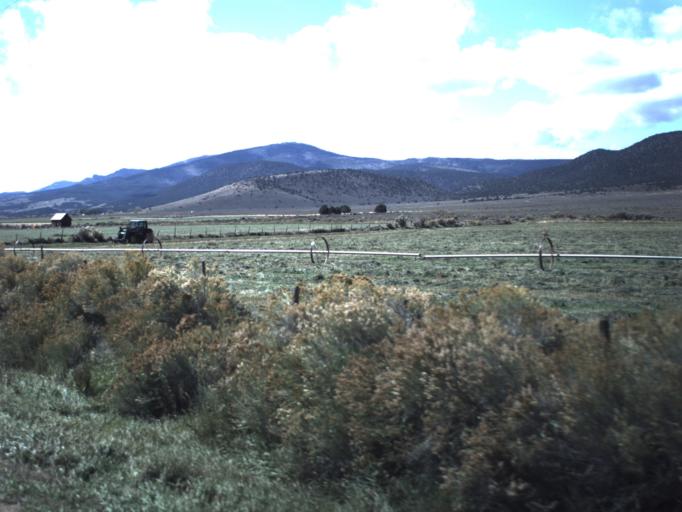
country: US
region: Utah
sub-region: Sevier County
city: Monroe
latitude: 38.4579
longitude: -111.9109
